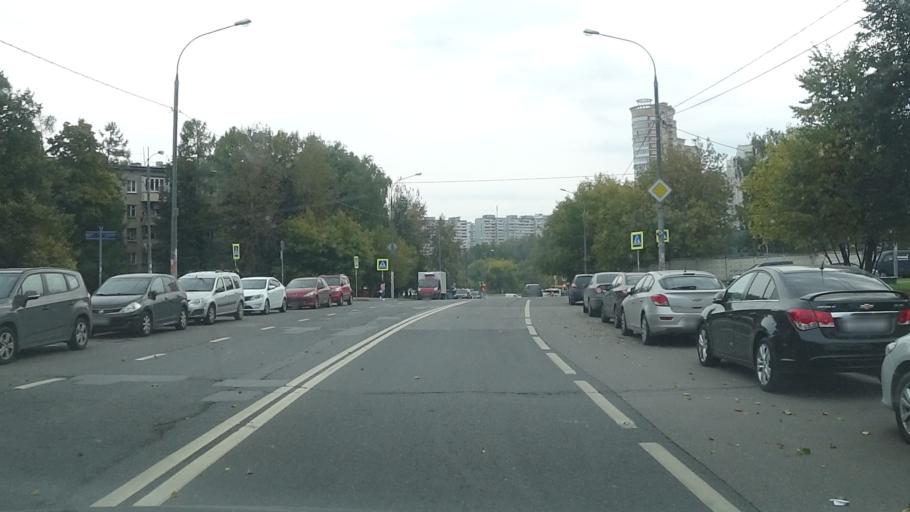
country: RU
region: Moscow
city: Solntsevo
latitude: 55.6542
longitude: 37.3863
